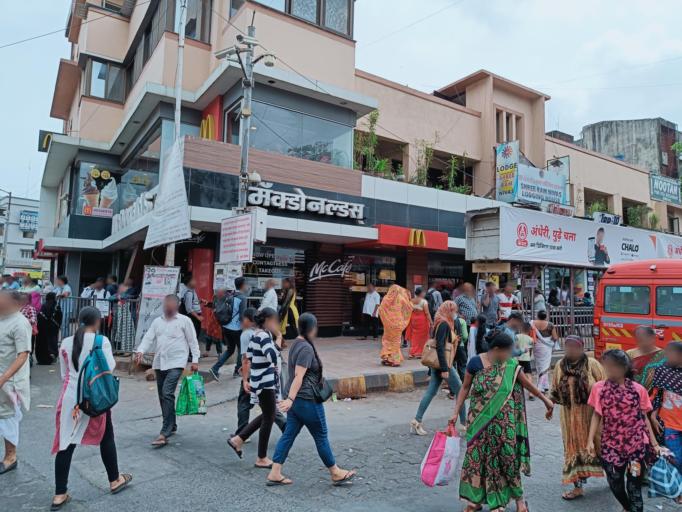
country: IN
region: Maharashtra
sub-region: Mumbai Suburban
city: Powai
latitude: 19.1197
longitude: 72.8462
